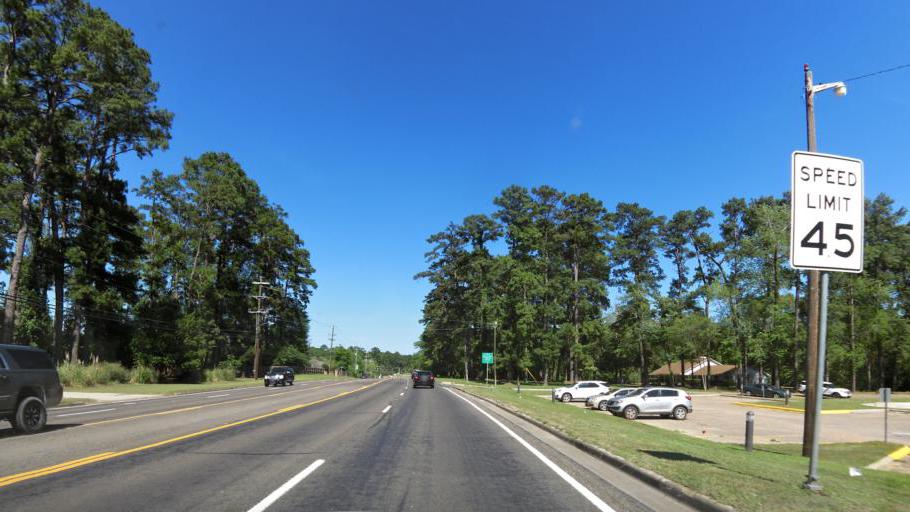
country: US
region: Texas
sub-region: Polk County
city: Livingston
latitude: 30.7106
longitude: -94.9269
